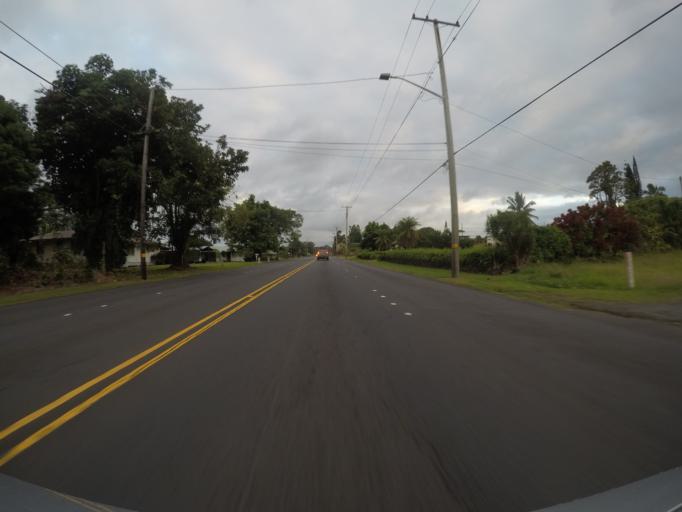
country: US
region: Hawaii
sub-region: Hawaii County
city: Hilo
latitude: 19.6809
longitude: -155.0672
